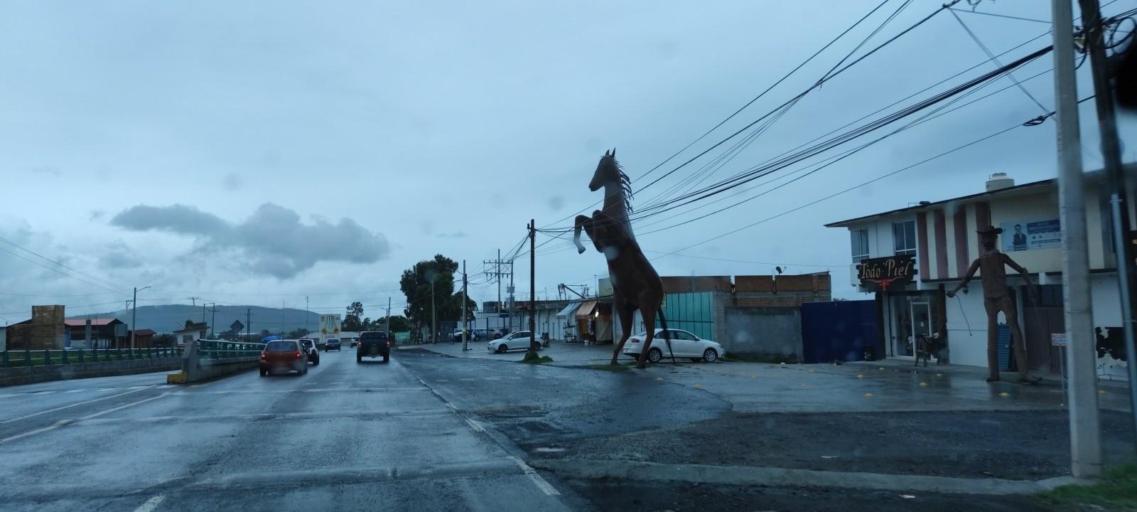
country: MX
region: Mexico
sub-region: Jilotepec
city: Jilotepec de Molina Enriquez
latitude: 19.9512
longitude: -99.5493
